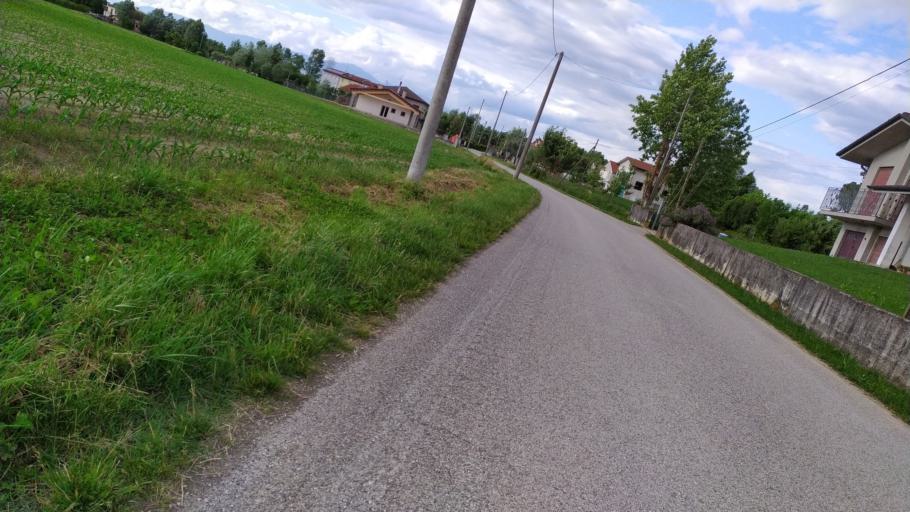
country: IT
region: Veneto
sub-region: Provincia di Padova
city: Villa del Conte
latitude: 45.5914
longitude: 11.8519
